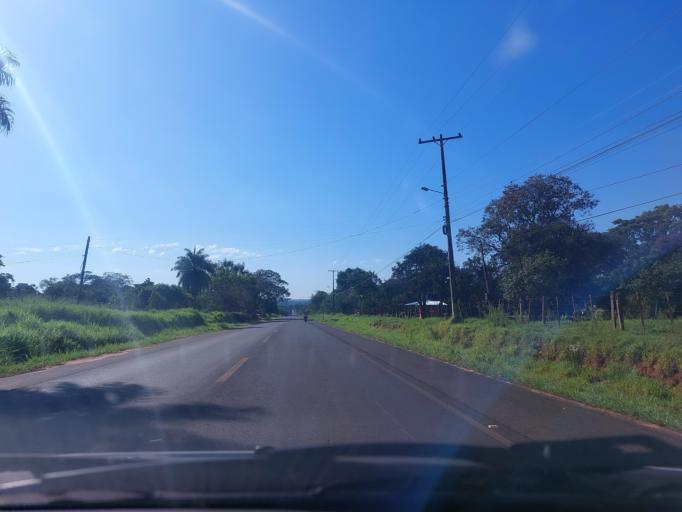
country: PY
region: San Pedro
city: Guayaybi
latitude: -24.5312
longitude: -56.4218
